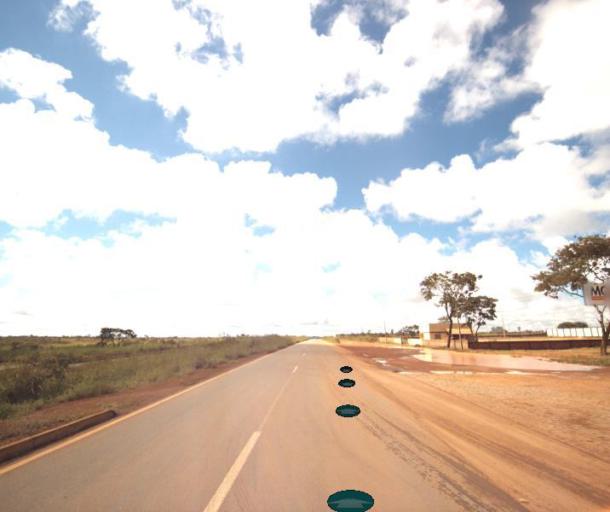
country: BR
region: Goias
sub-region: Anapolis
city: Anapolis
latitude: -16.2550
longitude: -48.9918
